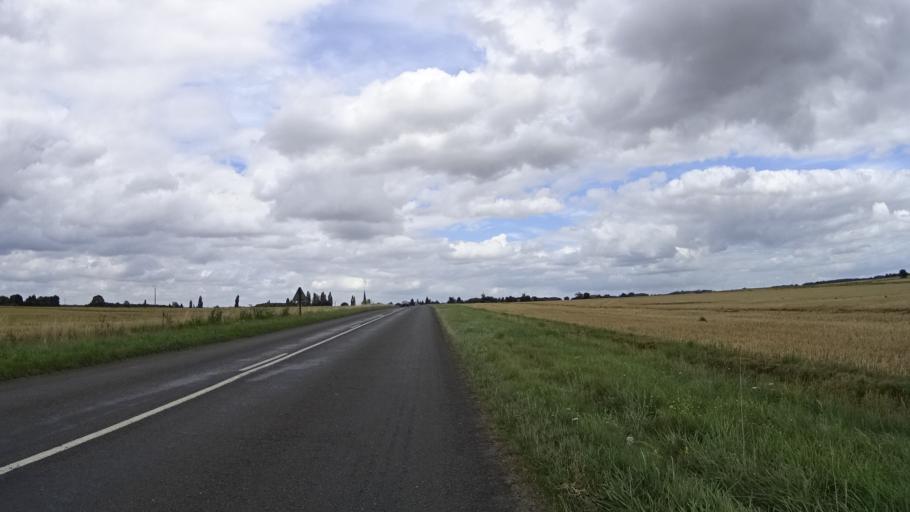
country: FR
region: Centre
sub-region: Departement du Loiret
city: Douchy
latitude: 47.9630
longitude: 3.0655
